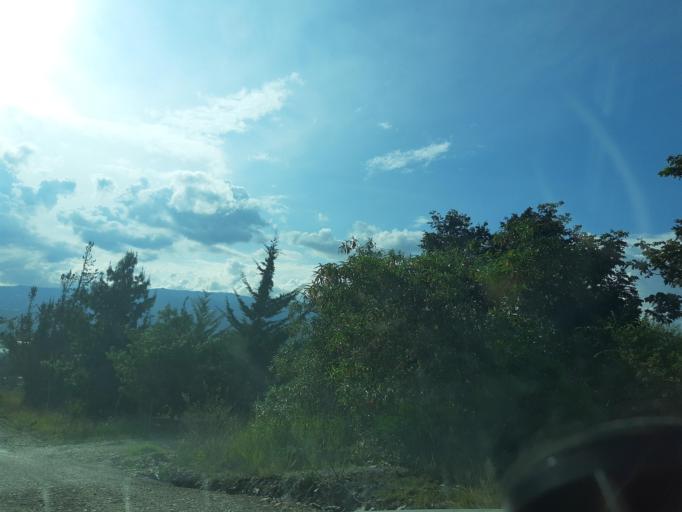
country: CO
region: Boyaca
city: Villa de Leiva
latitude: 5.6657
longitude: -73.5626
